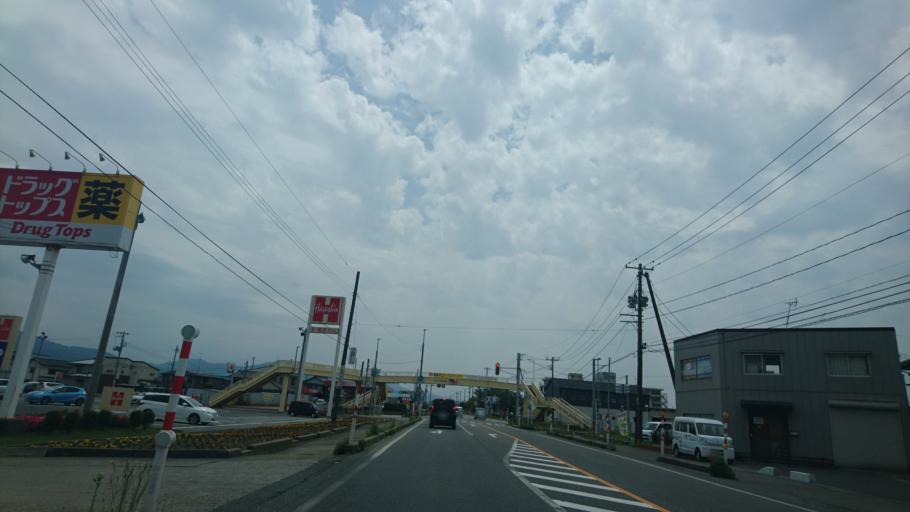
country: JP
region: Niigata
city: Murakami
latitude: 38.1158
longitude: 139.4507
